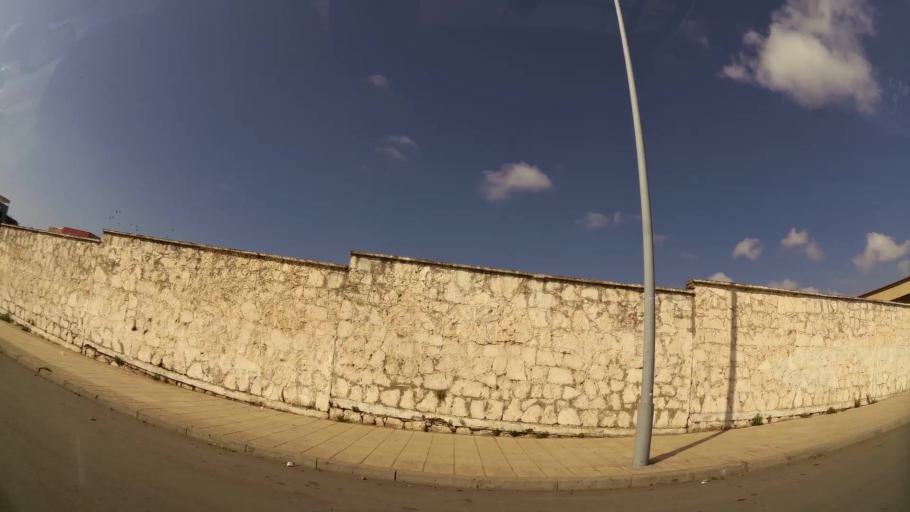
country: MA
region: Rabat-Sale-Zemmour-Zaer
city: Sale
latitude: 34.0491
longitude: -6.7875
